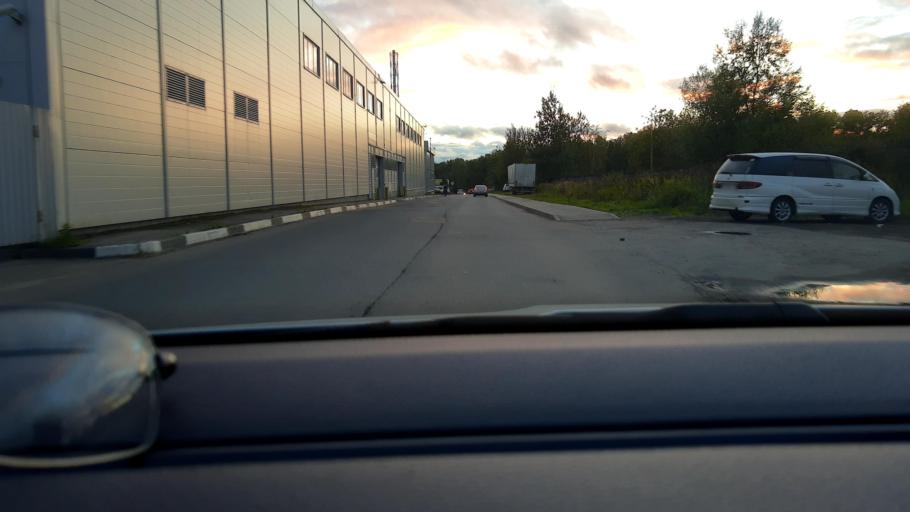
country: RU
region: Moskovskaya
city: Arkhangel'skoye
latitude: 55.8047
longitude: 37.2972
